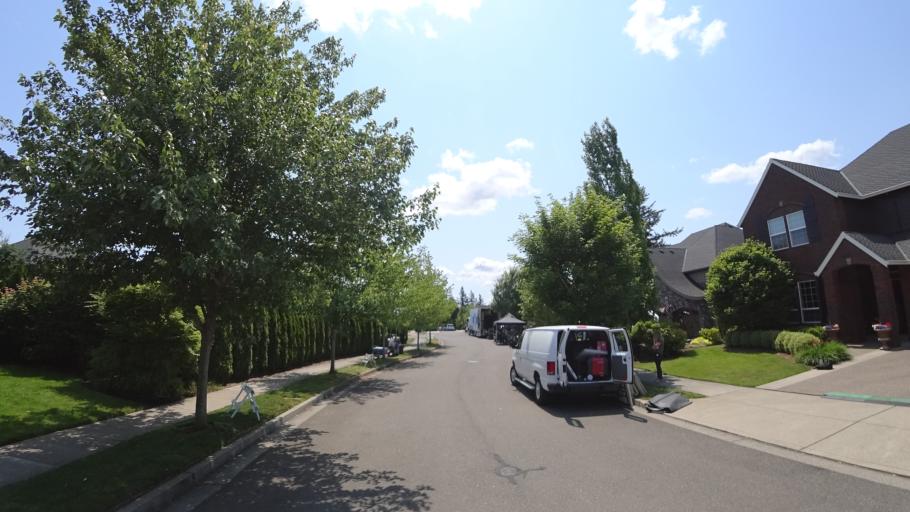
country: US
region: Oregon
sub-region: Clackamas County
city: Happy Valley
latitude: 45.4460
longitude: -122.5477
